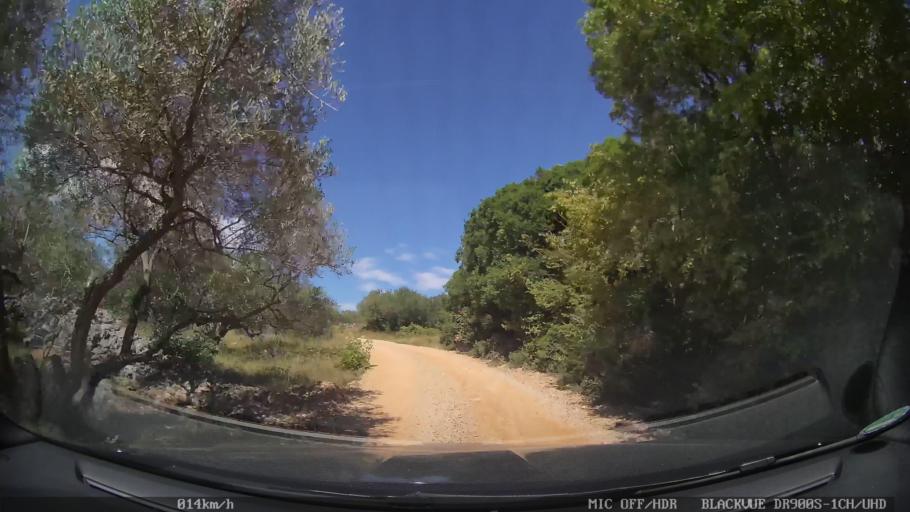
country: HR
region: Primorsko-Goranska
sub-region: Grad Krk
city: Krk
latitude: 45.0259
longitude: 14.5234
